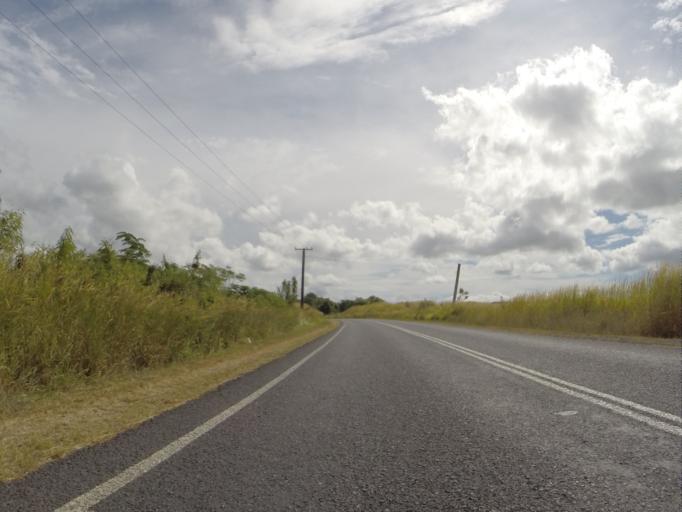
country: FJ
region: Western
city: Nadi
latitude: -18.1077
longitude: 177.4045
